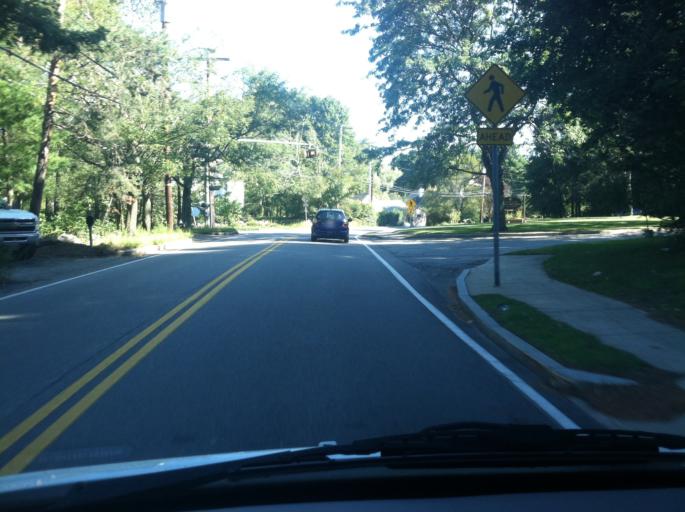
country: US
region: Massachusetts
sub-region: Middlesex County
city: Bedford
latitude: 42.4918
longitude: -71.2906
